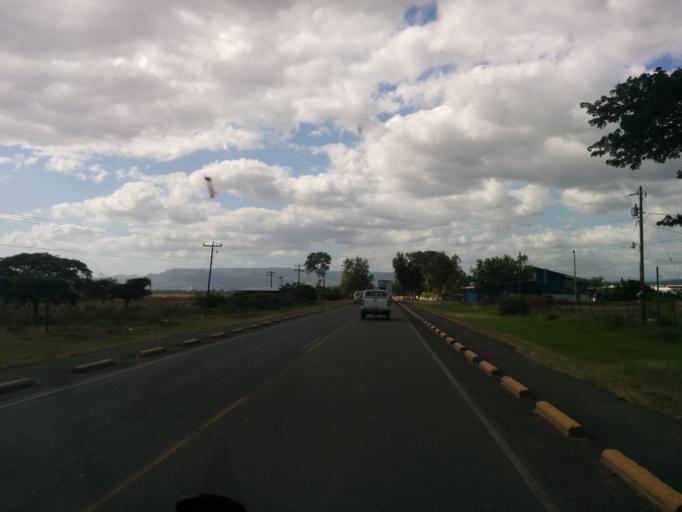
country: NI
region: Matagalpa
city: Ciudad Dario
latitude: 12.8610
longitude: -86.1079
